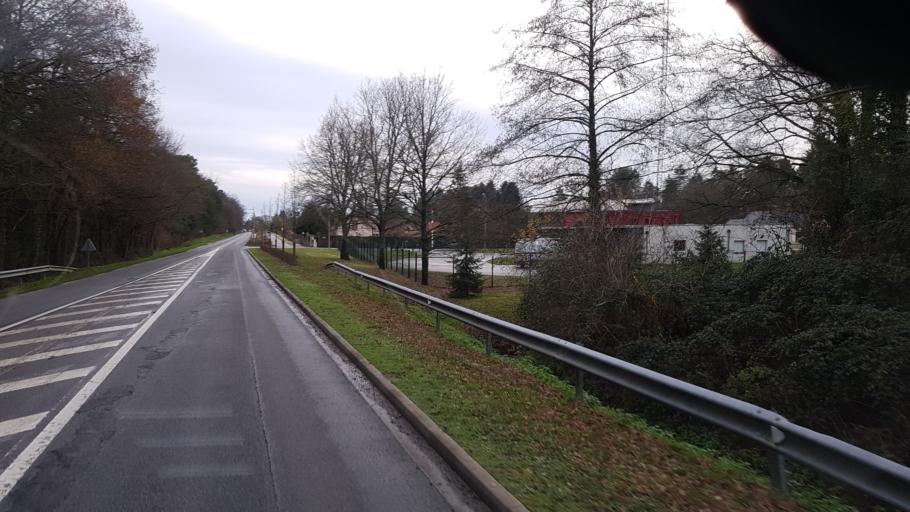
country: FR
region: Centre
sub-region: Departement du Loir-et-Cher
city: Nouan-le-Fuzelier
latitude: 47.5479
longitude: 2.0353
